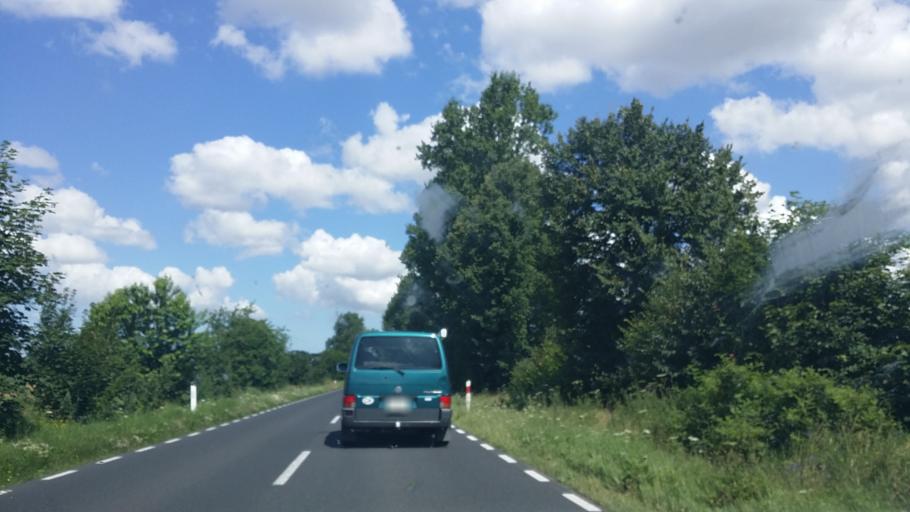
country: PL
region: West Pomeranian Voivodeship
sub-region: Powiat kolobrzeski
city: Goscino
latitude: 53.9893
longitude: 15.6744
